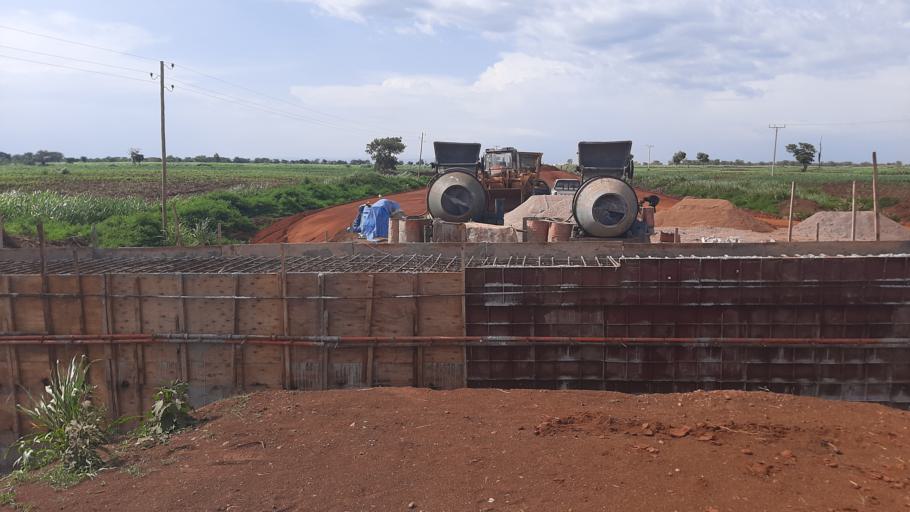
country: ET
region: Gambela
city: Gambela
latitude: 7.9692
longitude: 34.5583
